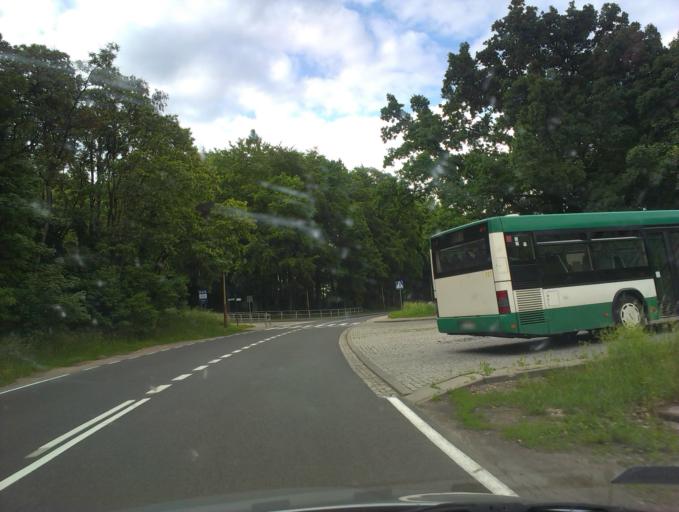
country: PL
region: West Pomeranian Voivodeship
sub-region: Powiat szczecinecki
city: Szczecinek
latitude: 53.6843
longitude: 16.6887
